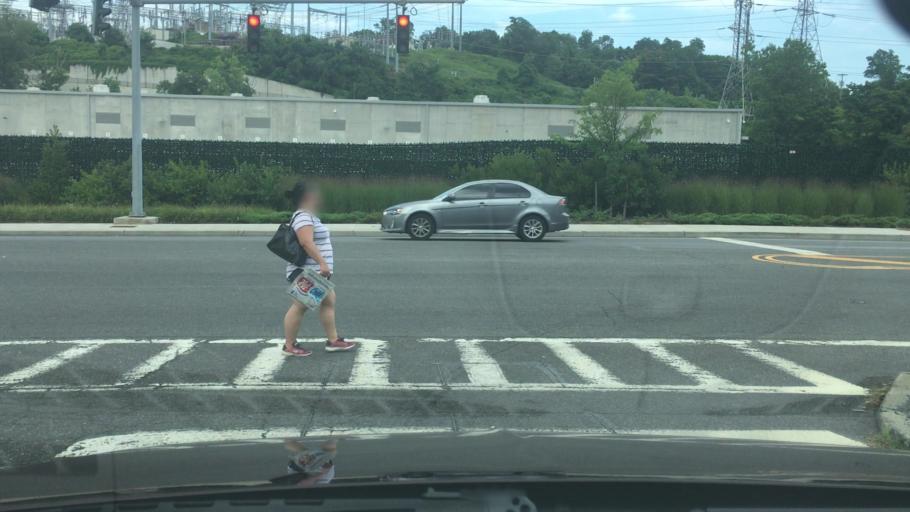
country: US
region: New York
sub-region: Westchester County
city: Bronxville
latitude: 40.9537
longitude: -73.8578
